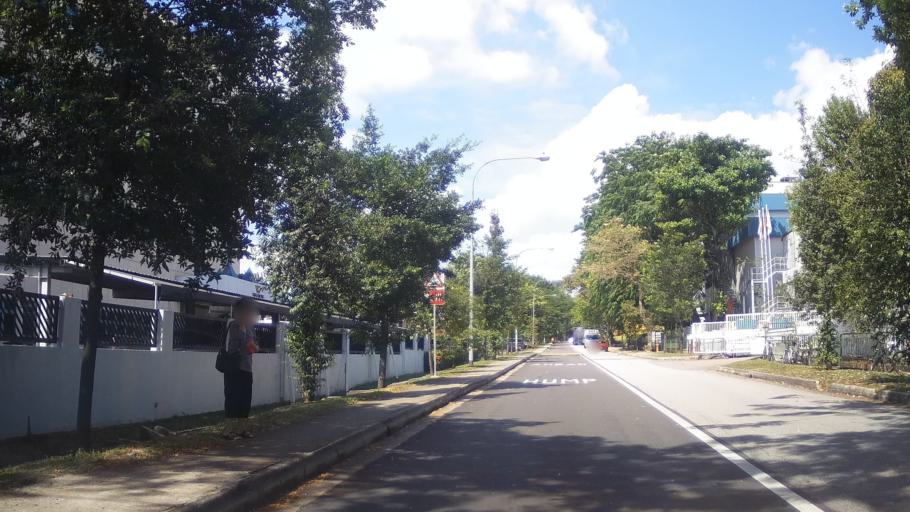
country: SG
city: Singapore
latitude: 1.3203
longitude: 103.7139
